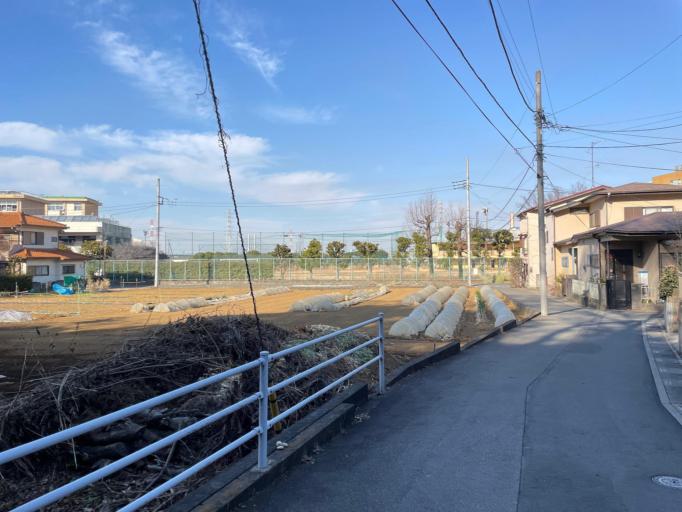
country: JP
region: Saitama
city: Wako
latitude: 35.7958
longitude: 139.6290
